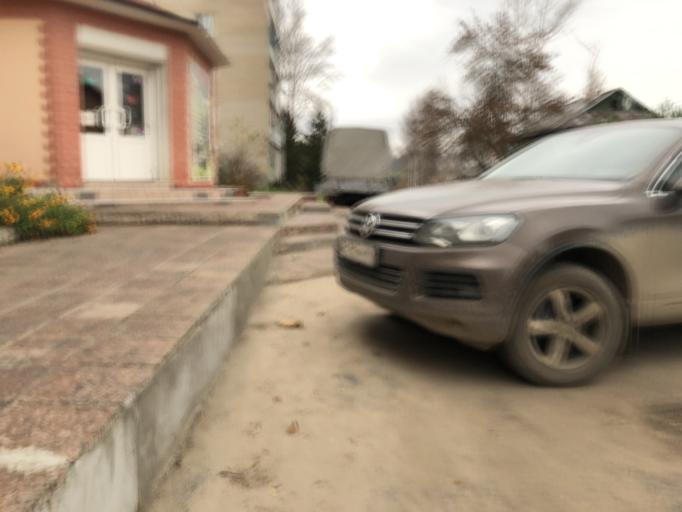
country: RU
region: Tverskaya
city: Rzhev
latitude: 56.2580
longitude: 34.3247
